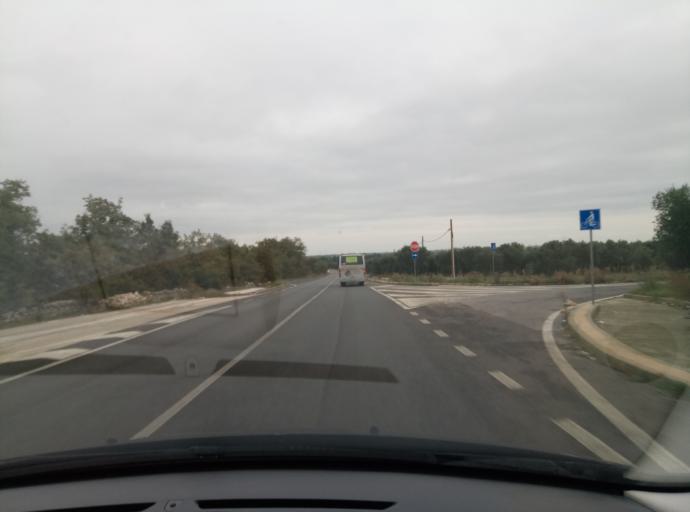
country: IT
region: Apulia
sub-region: Provincia di Bari
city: Acquaviva delle Fonti
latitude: 40.8734
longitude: 16.8073
